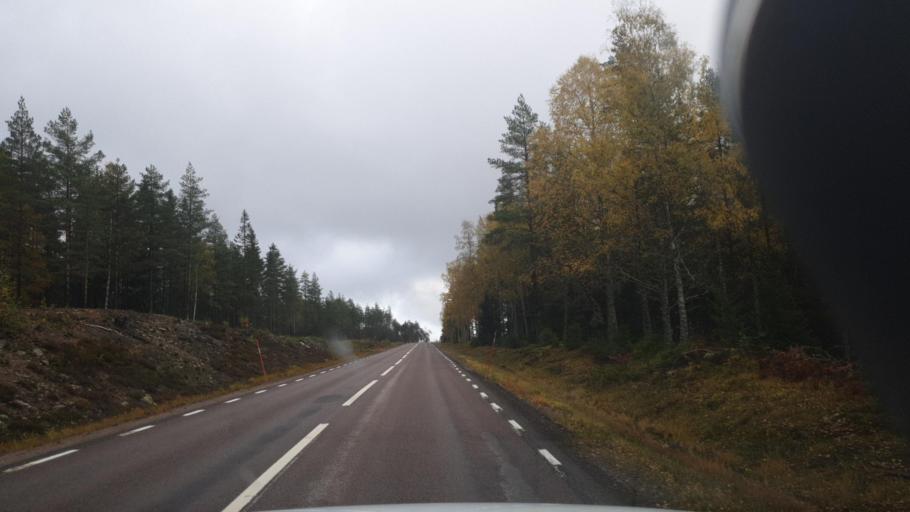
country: SE
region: Vaermland
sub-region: Sunne Kommun
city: Sunne
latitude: 59.6896
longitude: 13.0515
